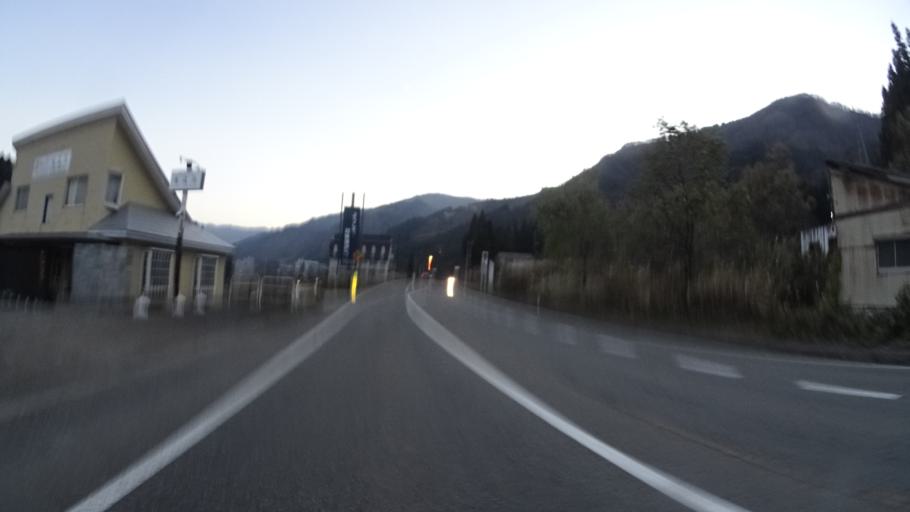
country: JP
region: Niigata
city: Shiozawa
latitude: 36.9637
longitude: 138.8011
